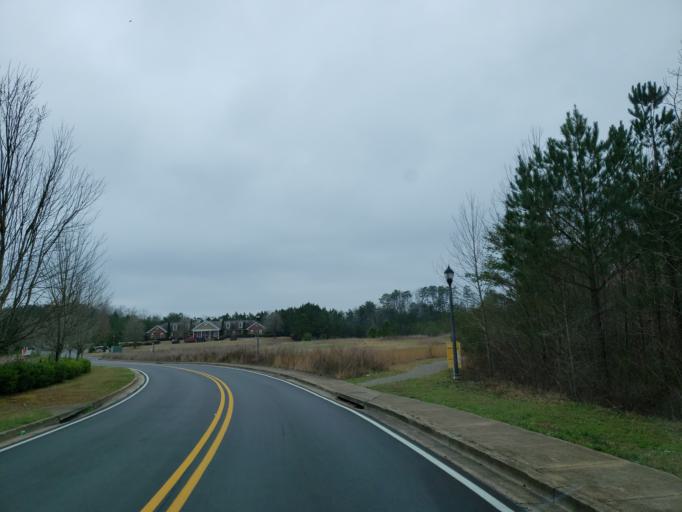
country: US
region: Georgia
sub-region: Pickens County
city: Jasper
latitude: 34.4449
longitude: -84.4473
